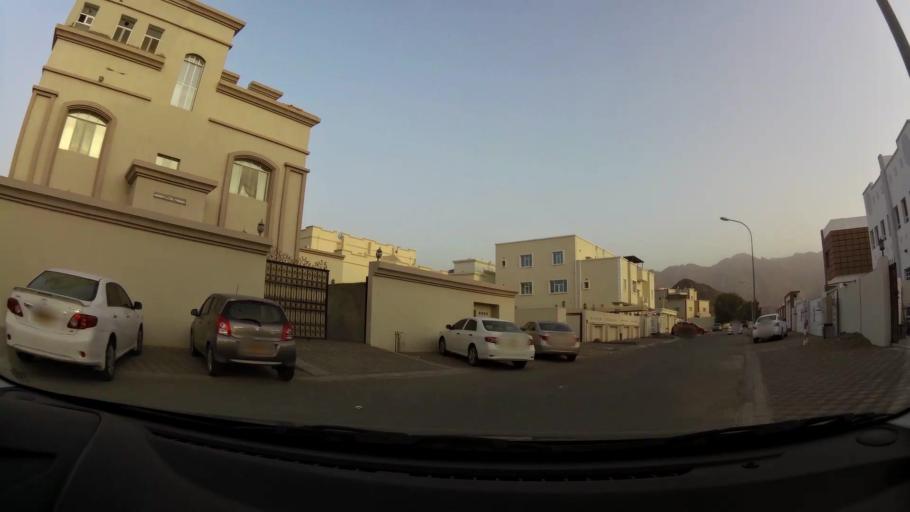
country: OM
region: Muhafazat Masqat
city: Bawshar
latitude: 23.4874
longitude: 58.3156
